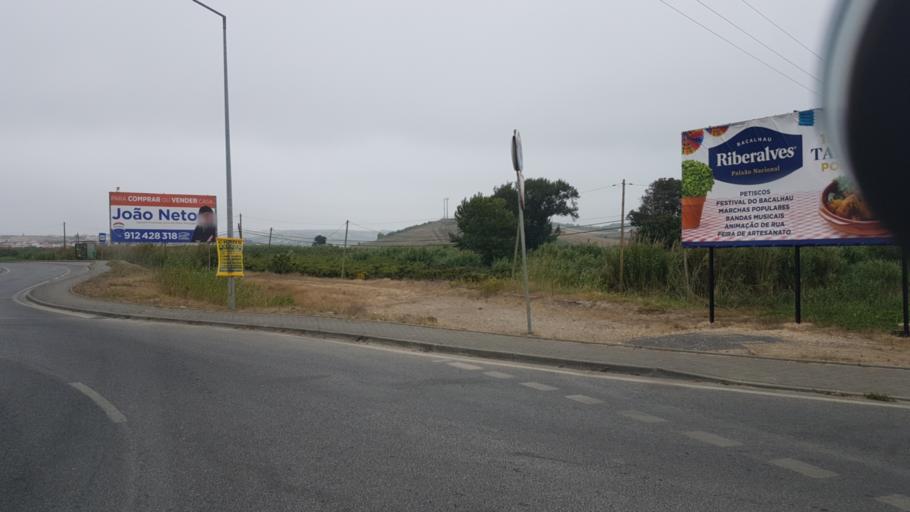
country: PT
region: Lisbon
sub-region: Torres Vedras
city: Silveira
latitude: 39.0892
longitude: -9.3342
